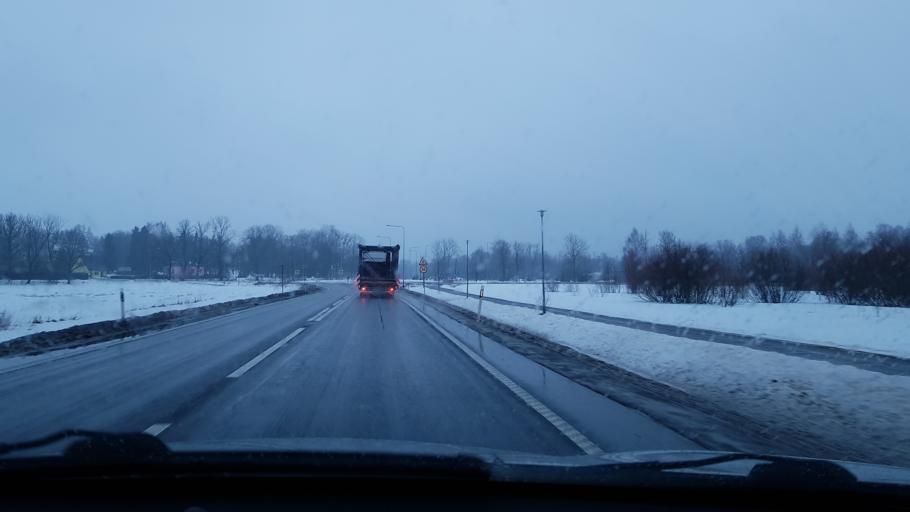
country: EE
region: Jaervamaa
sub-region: Tueri vald
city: Tueri
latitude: 58.8457
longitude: 25.4778
